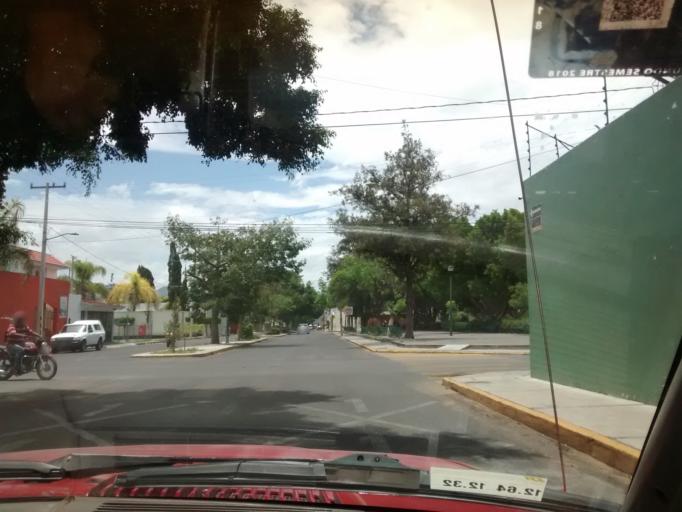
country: MX
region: Puebla
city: Tehuacan
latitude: 18.4624
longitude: -97.4064
